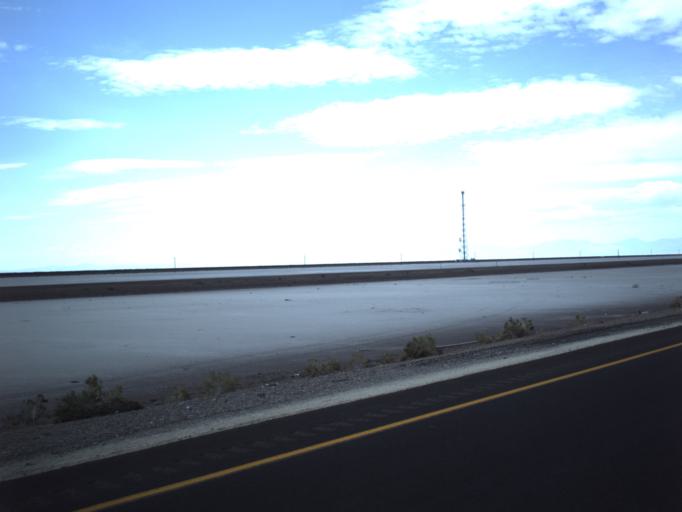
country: US
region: Utah
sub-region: Tooele County
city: Wendover
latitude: 40.7330
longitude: -113.5510
